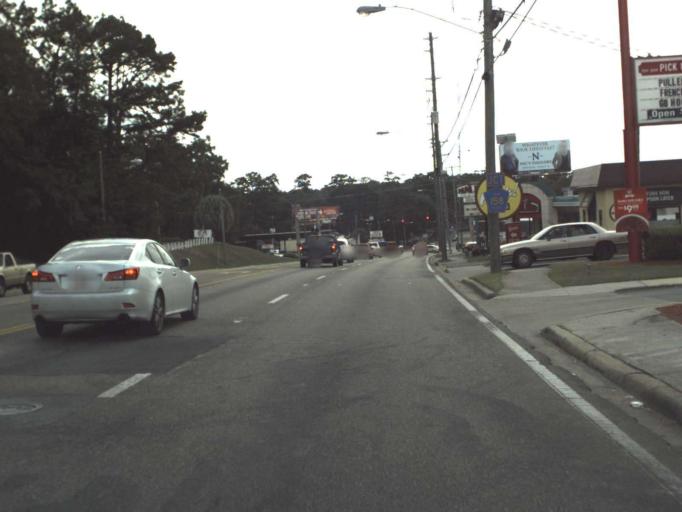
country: US
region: Florida
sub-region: Leon County
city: Tallahassee
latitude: 30.4650
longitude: -84.2833
